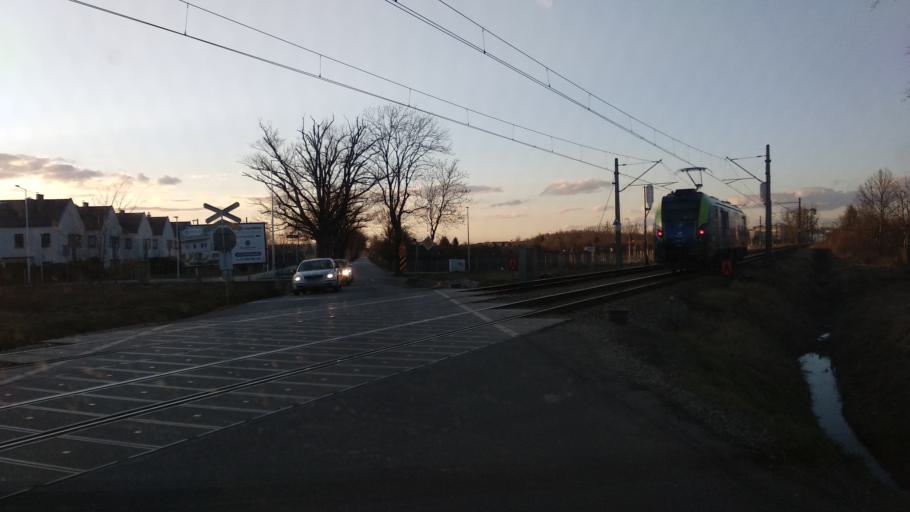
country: PL
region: Lower Silesian Voivodeship
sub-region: Powiat wroclawski
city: Zerniki Wroclawskie
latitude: 51.0644
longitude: 17.0682
